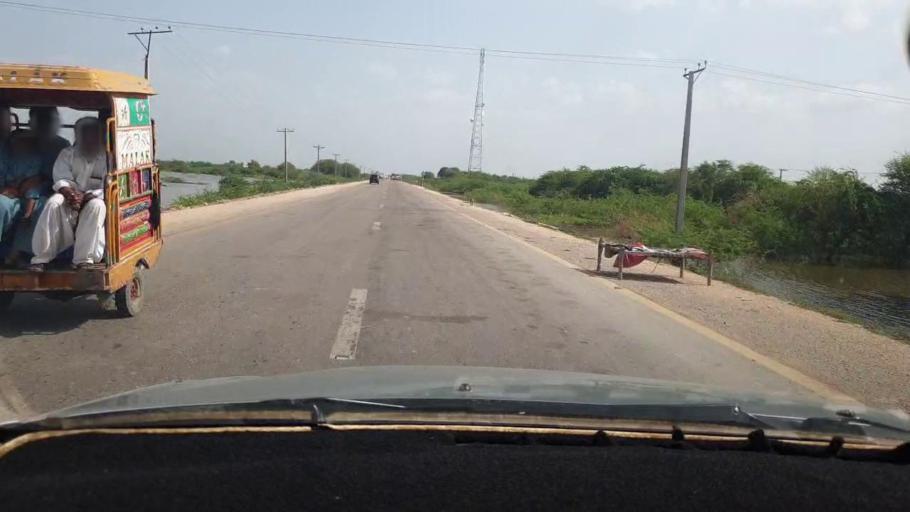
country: PK
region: Sindh
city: Naukot
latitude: 24.9103
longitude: 69.3255
